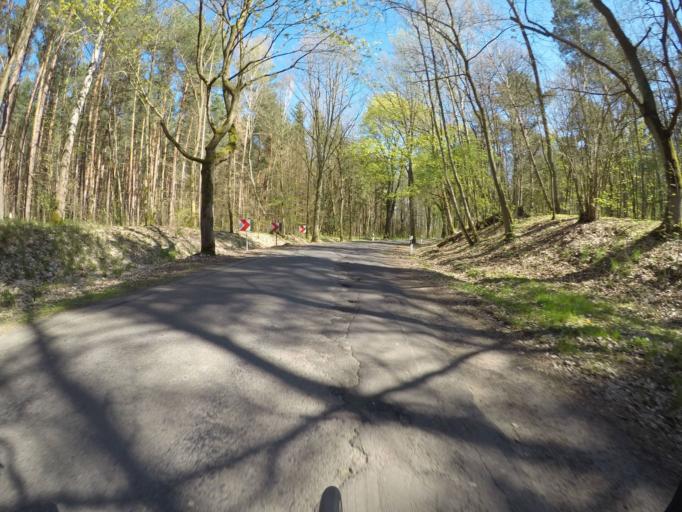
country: DE
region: Brandenburg
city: Werftpfuhl
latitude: 52.6204
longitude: 13.8400
